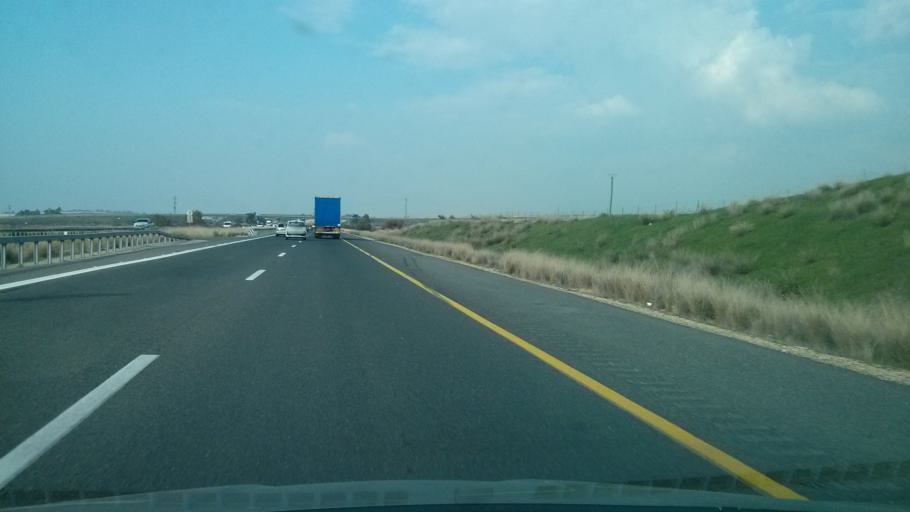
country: IL
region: Central District
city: Bene 'Ayish
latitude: 31.7393
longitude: 34.8225
